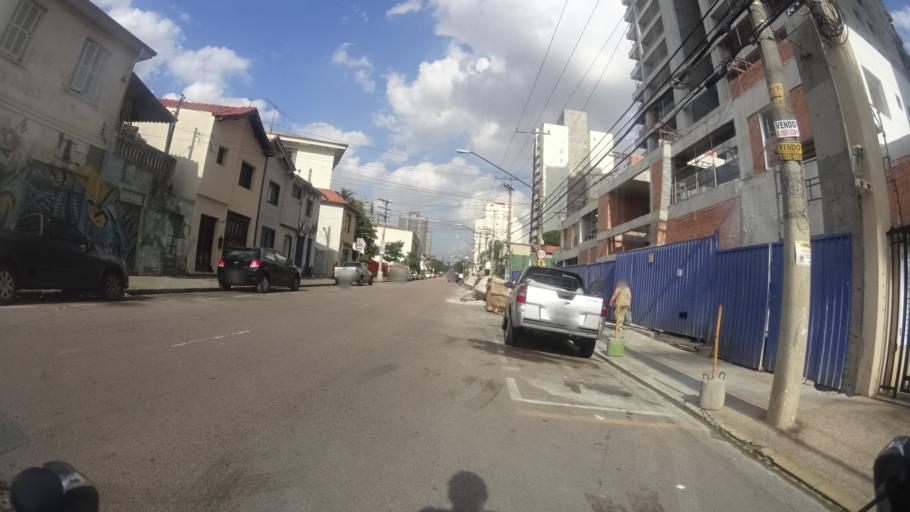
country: BR
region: Sao Paulo
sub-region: Sao Paulo
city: Sao Paulo
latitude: -23.5564
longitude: -46.5990
